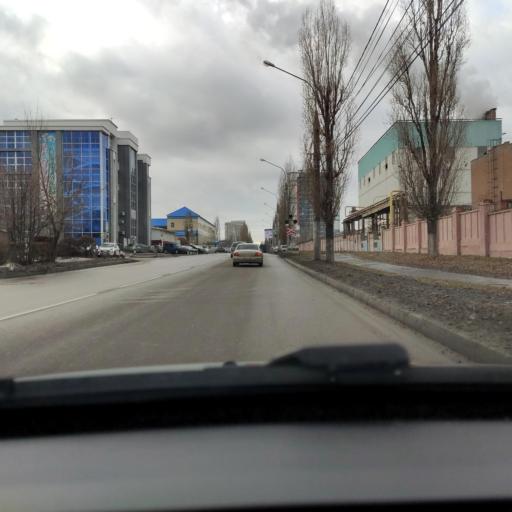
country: RU
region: Voronezj
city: Voronezh
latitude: 51.6599
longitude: 39.1612
